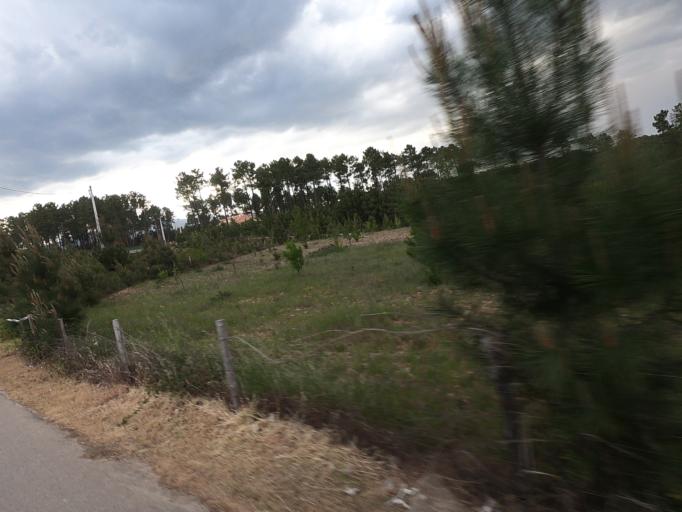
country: PT
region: Vila Real
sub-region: Vila Real
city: Vila Real
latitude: 41.2703
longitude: -7.6901
